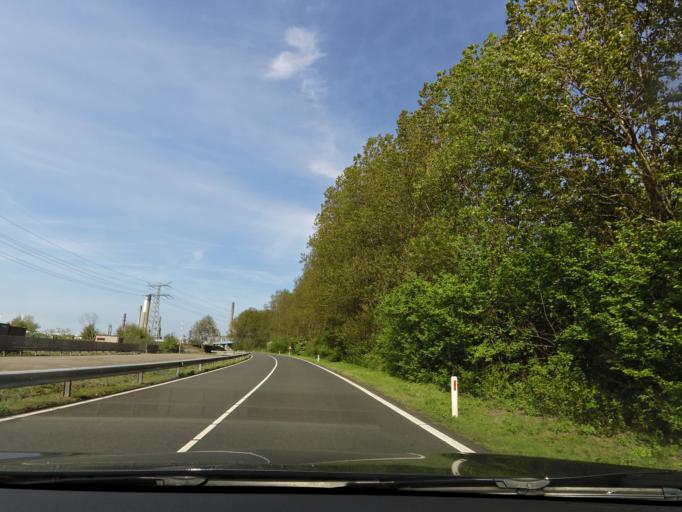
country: NL
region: South Holland
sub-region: Gemeente Rotterdam
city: Hoek van Holland
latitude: 51.9345
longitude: 4.1042
